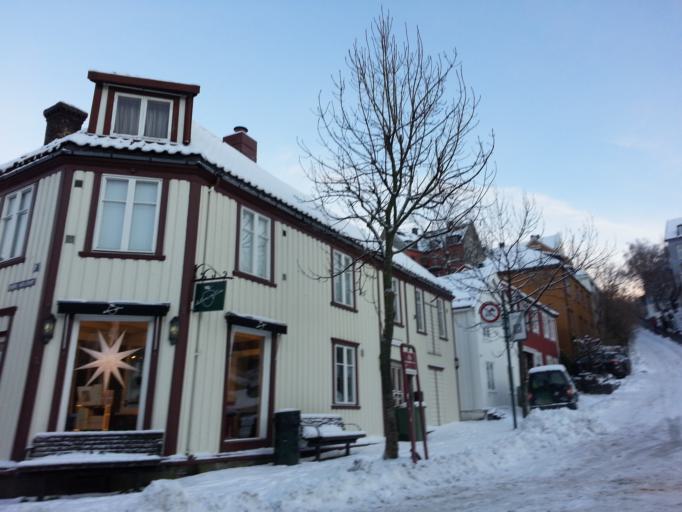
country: NO
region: Sor-Trondelag
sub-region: Trondheim
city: Trondheim
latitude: 63.4281
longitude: 10.4029
